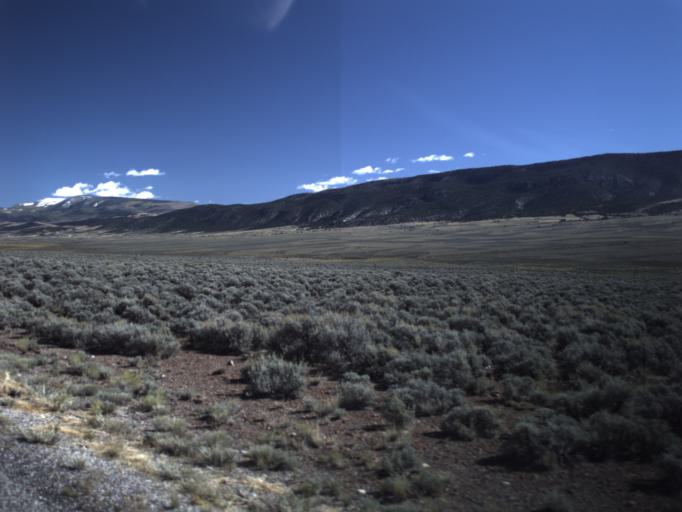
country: US
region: Utah
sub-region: Wayne County
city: Loa
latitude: 38.3744
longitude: -111.9378
